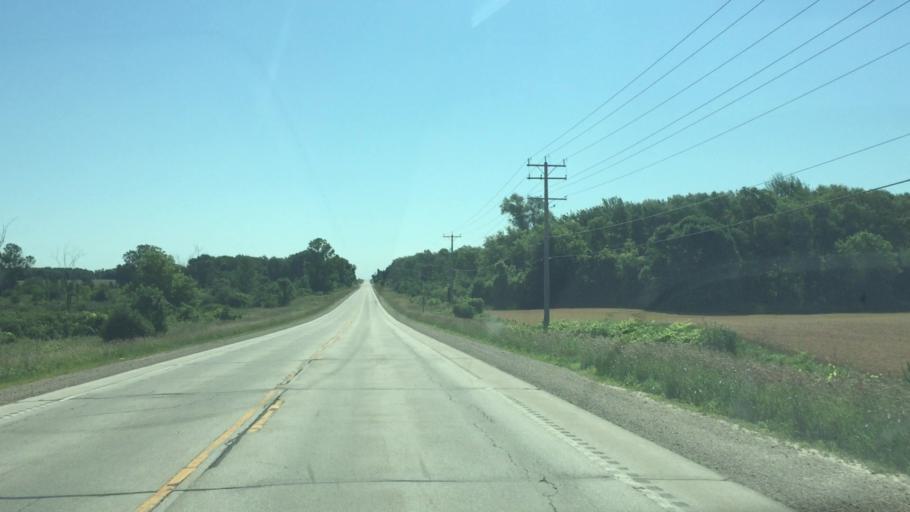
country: US
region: Wisconsin
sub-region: Calumet County
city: Sherwood
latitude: 44.1409
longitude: -88.2558
